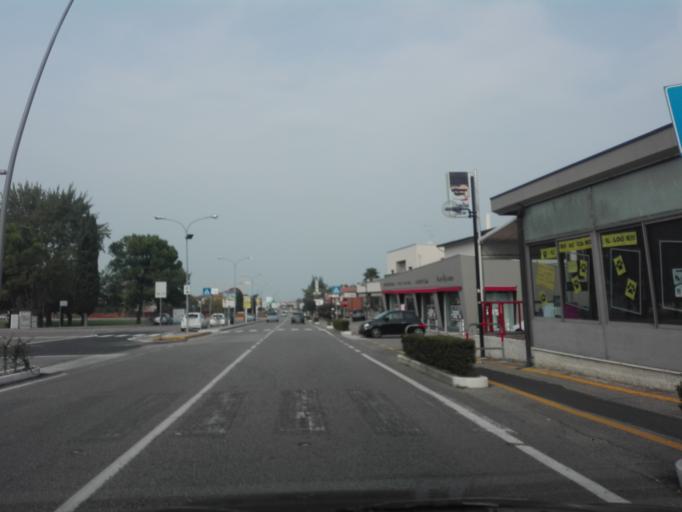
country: IT
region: Veneto
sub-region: Provincia di Verona
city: Peschiera del Garda
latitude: 45.4483
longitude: 10.6672
